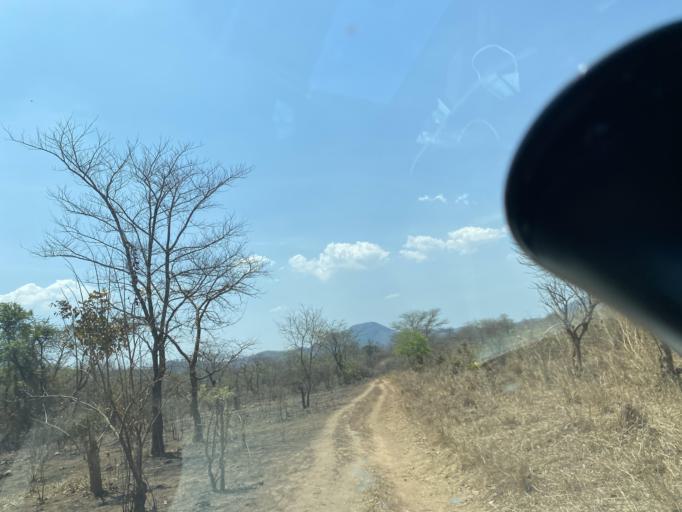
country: ZM
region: Lusaka
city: Kafue
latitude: -15.7756
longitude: 28.4581
